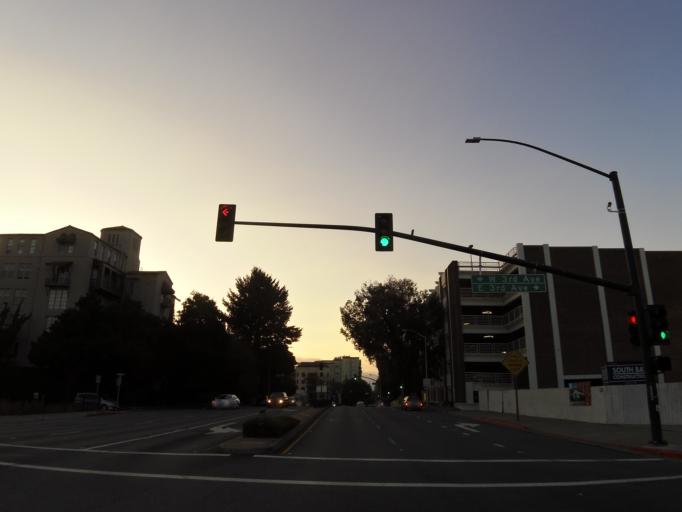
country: US
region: California
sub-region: San Mateo County
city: San Mateo
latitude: 37.5630
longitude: -122.3260
